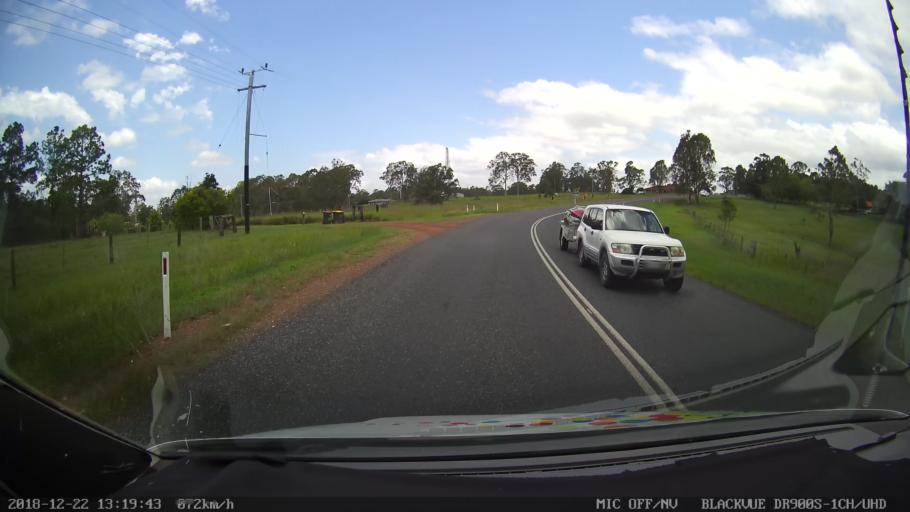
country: AU
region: New South Wales
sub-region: Clarence Valley
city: South Grafton
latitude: -29.7591
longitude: 152.9303
